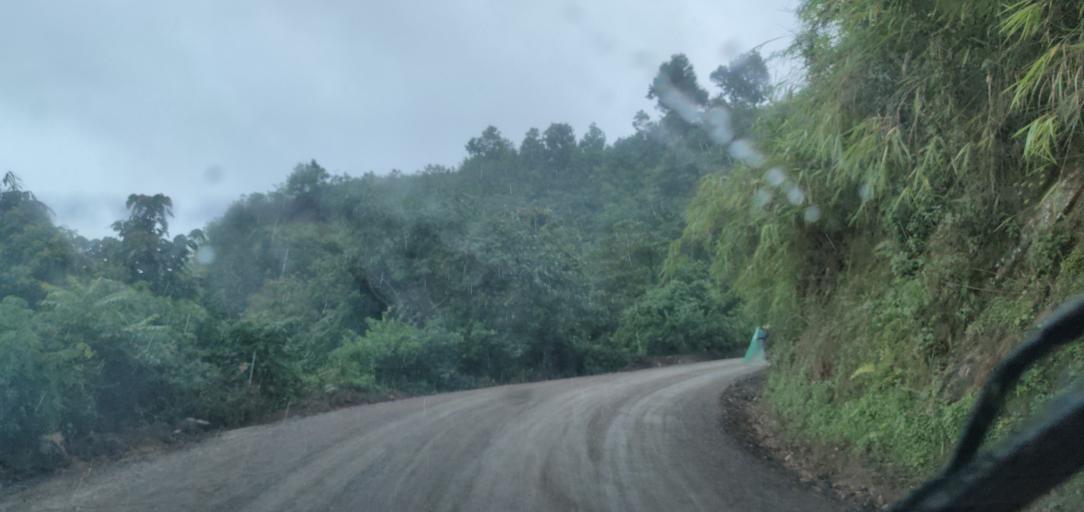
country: LA
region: Phongsali
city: Phongsali
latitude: 21.4298
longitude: 102.1606
